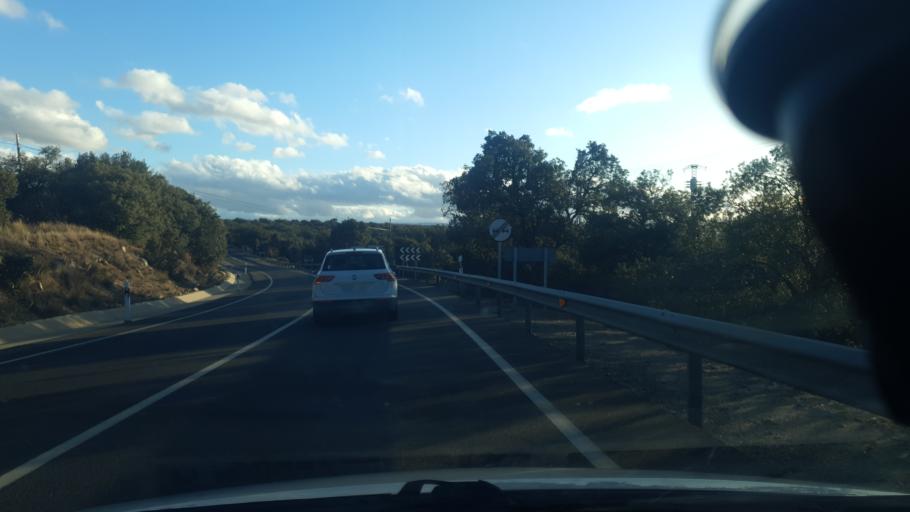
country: ES
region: Castille and Leon
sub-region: Provincia de Avila
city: Mingorria
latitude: 40.7164
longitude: -4.6743
